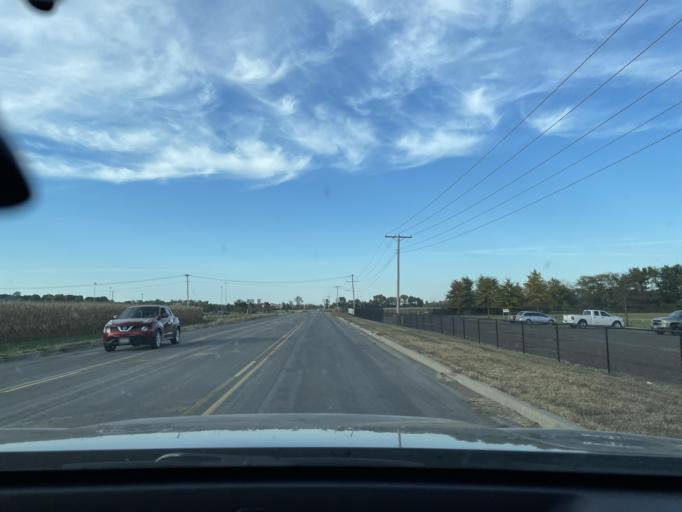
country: US
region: Missouri
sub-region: Andrew County
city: Country Club Village
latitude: 39.7908
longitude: -94.7678
